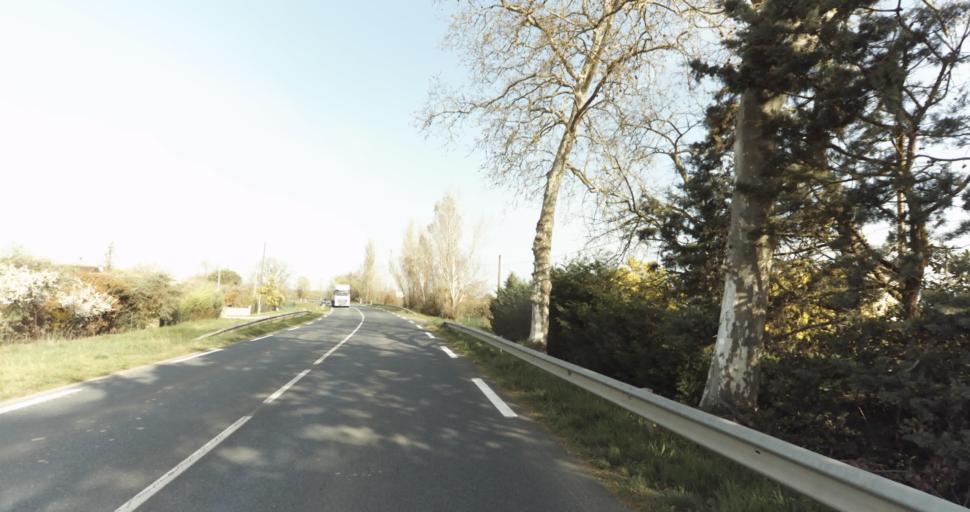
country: FR
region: Midi-Pyrenees
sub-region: Departement du Tarn
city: Giroussens
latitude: 43.7500
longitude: 1.7295
